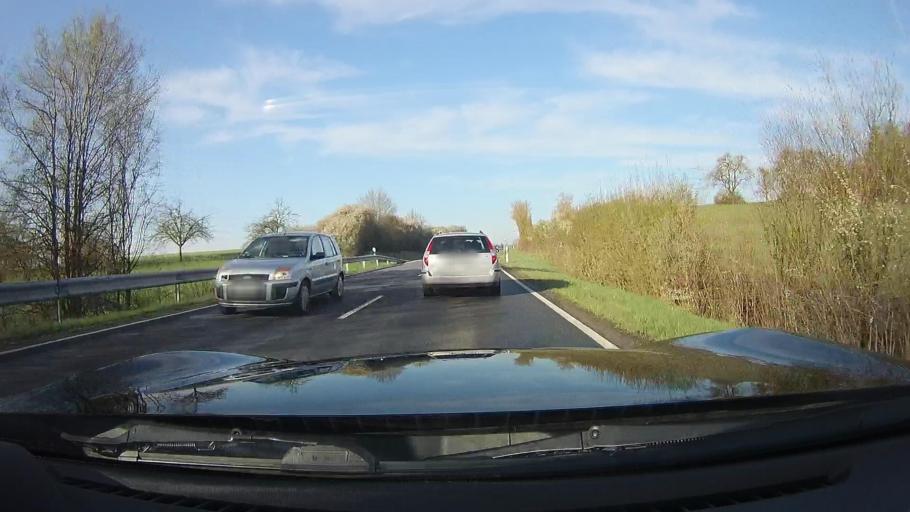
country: DE
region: Baden-Wuerttemberg
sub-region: Karlsruhe Region
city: Billigheim
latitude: 49.4087
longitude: 9.2674
